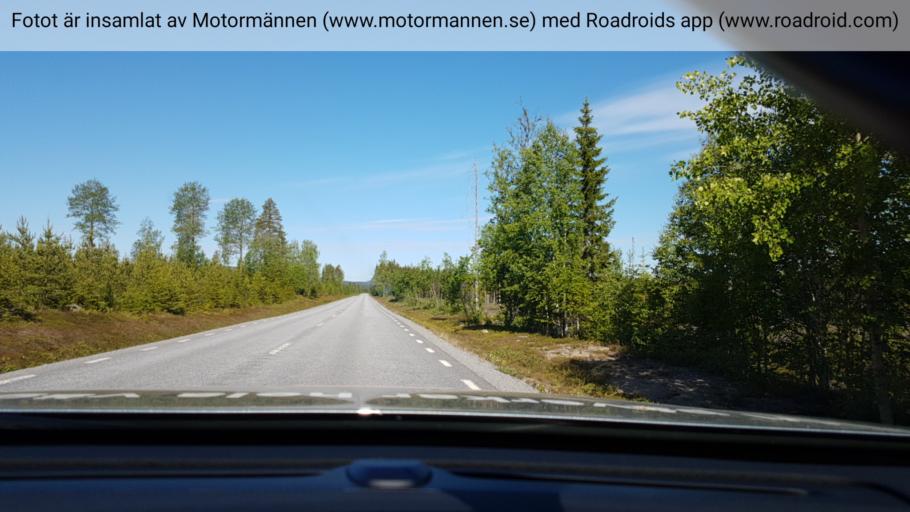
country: SE
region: Vaesterbotten
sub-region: Bjurholms Kommun
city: Bjurholm
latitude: 63.9550
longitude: 18.8795
